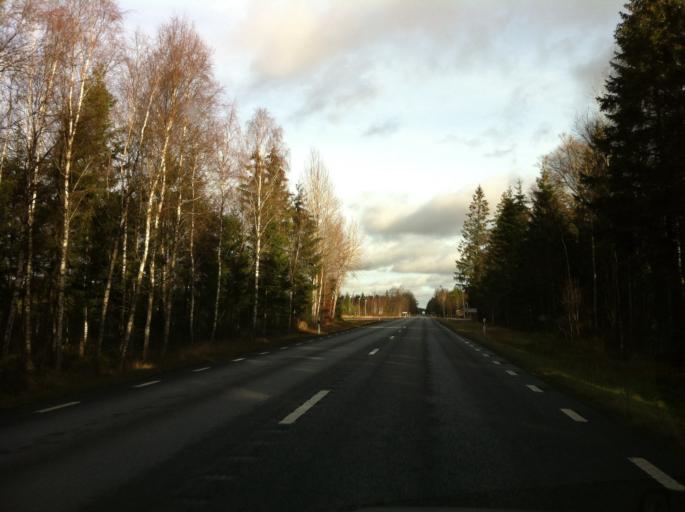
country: SE
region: Kronoberg
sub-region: Alvesta Kommun
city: Vislanda
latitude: 56.7487
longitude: 14.5145
